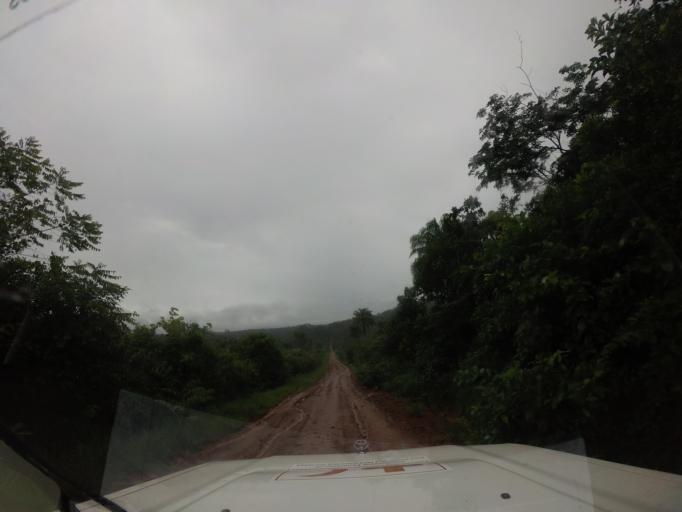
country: SL
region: Eastern Province
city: Kenema
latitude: 7.7321
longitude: -11.1887
